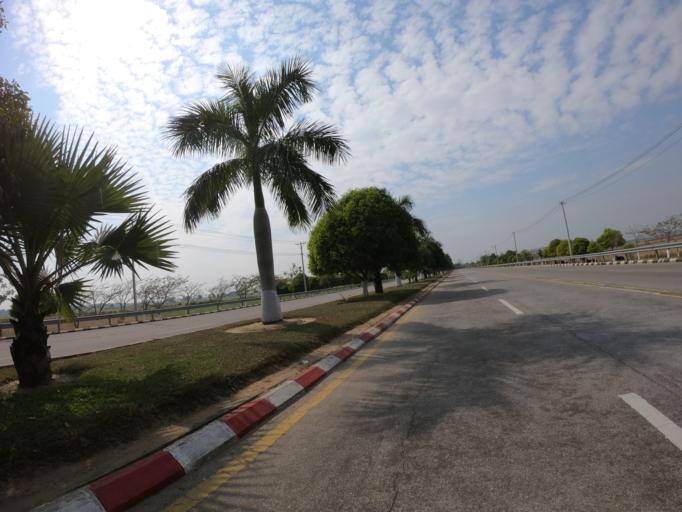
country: MM
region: Mandalay
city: Pyinmana
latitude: 19.6068
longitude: 96.1794
